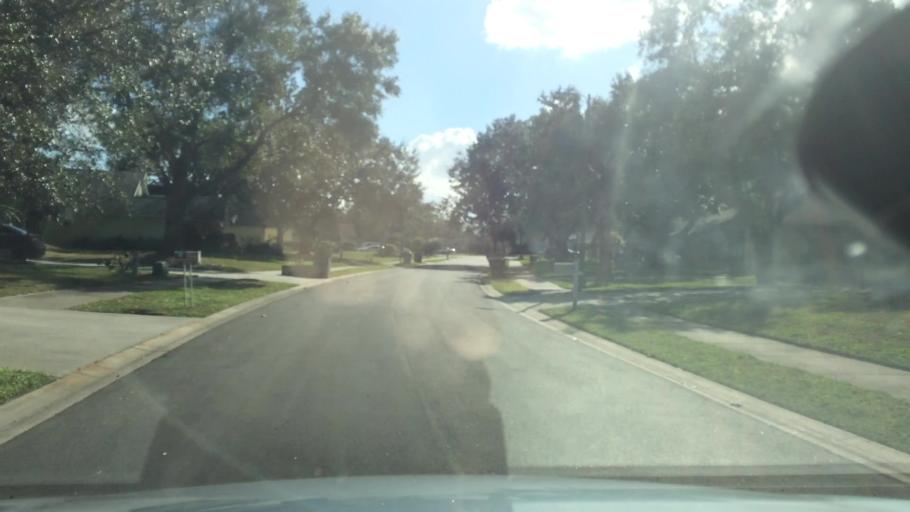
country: US
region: Florida
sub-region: Osceola County
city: Saint Cloud
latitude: 28.2148
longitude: -81.2840
